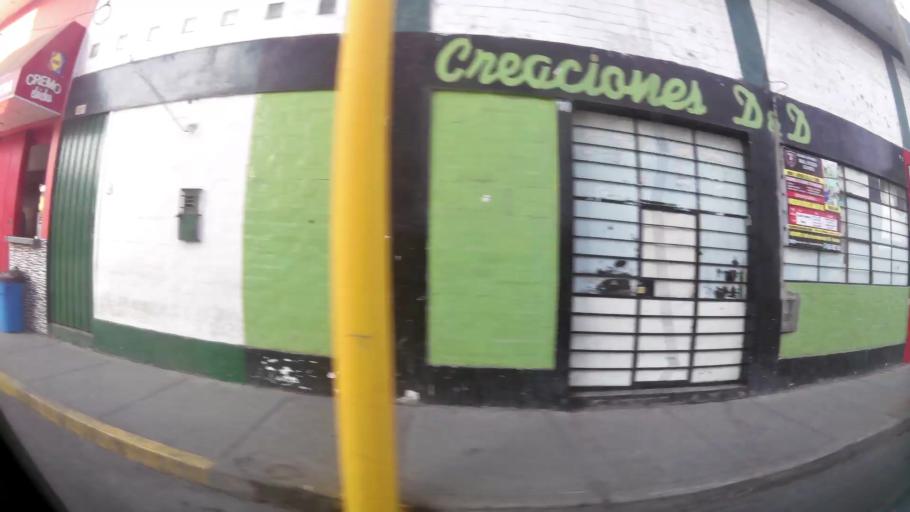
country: PE
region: Lima
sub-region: Huaura
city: Huacho
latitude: -11.1074
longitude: -77.6063
